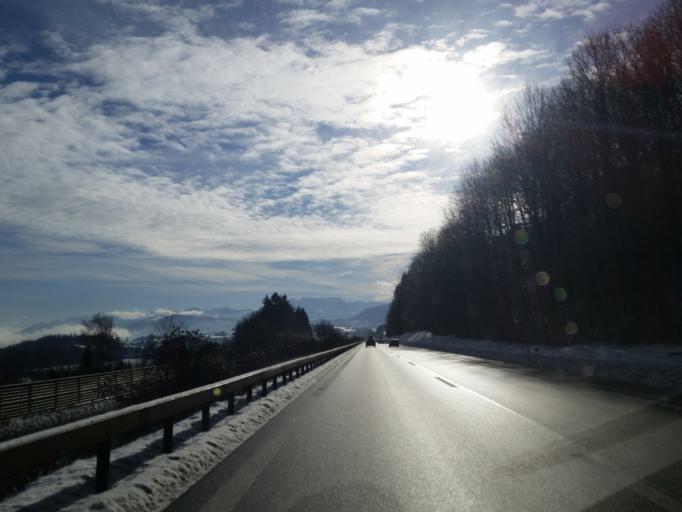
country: CH
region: Zurich
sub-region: Bezirk Horgen
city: Horgen / Allmend
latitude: 47.2452
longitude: 8.6018
